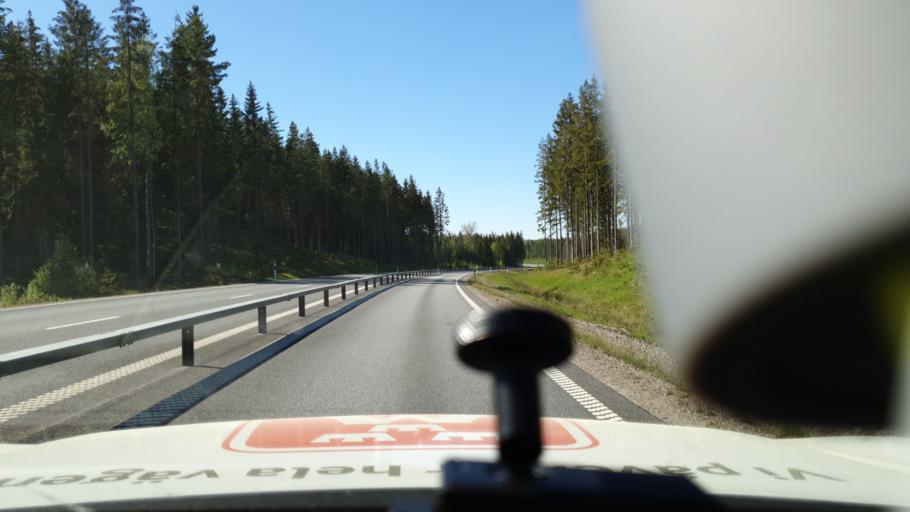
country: SE
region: Joenkoeping
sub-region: Vetlanda Kommun
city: Vetlanda
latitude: 57.4241
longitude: 15.1873
